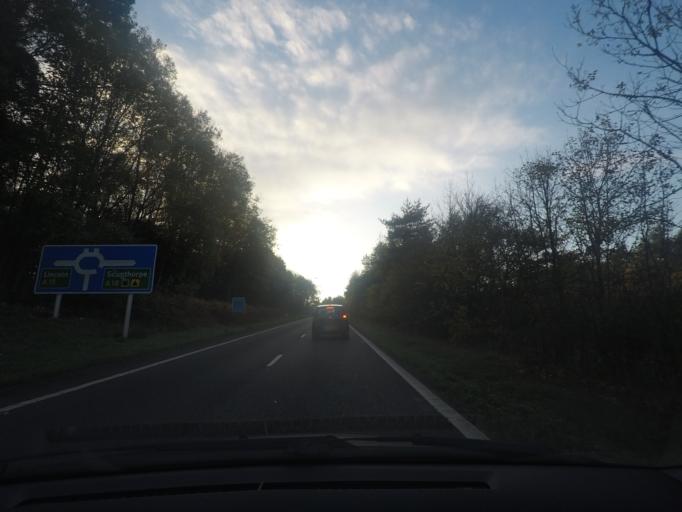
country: GB
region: England
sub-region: North Lincolnshire
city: Scawby
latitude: 53.5440
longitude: -0.5543
